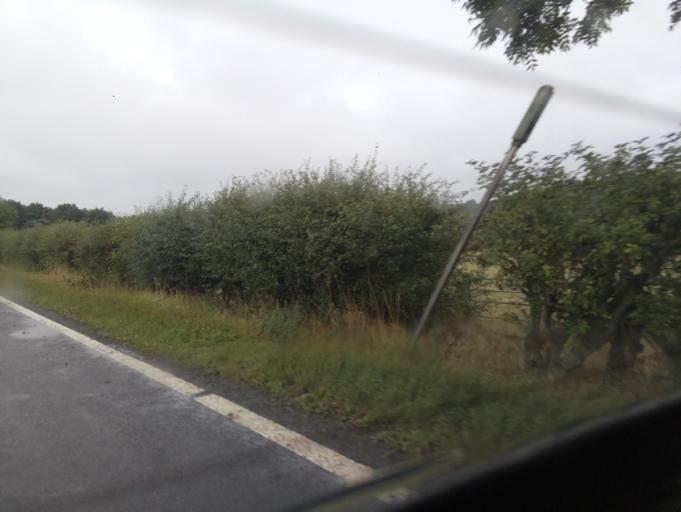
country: GB
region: England
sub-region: North Yorkshire
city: Pannal
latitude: 53.9278
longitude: -1.5352
